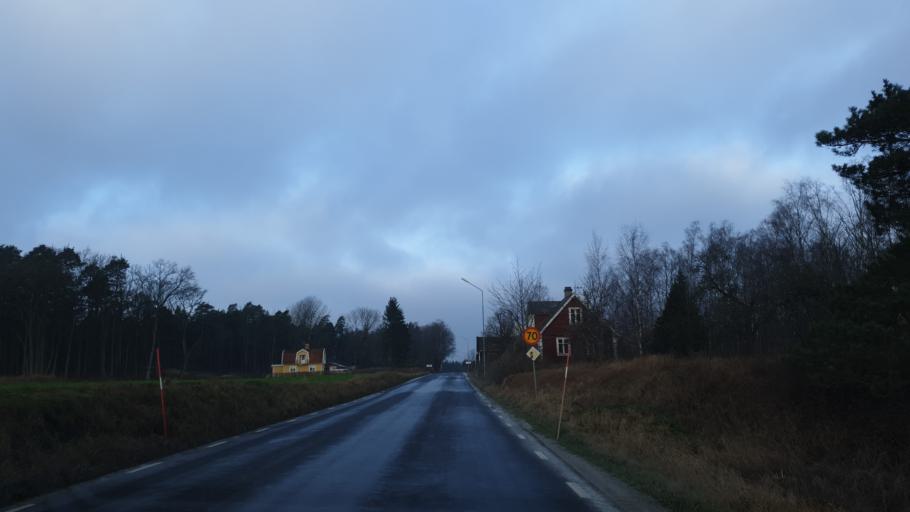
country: SE
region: Blekinge
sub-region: Karlshamns Kommun
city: Morrum
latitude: 56.1707
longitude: 14.7412
